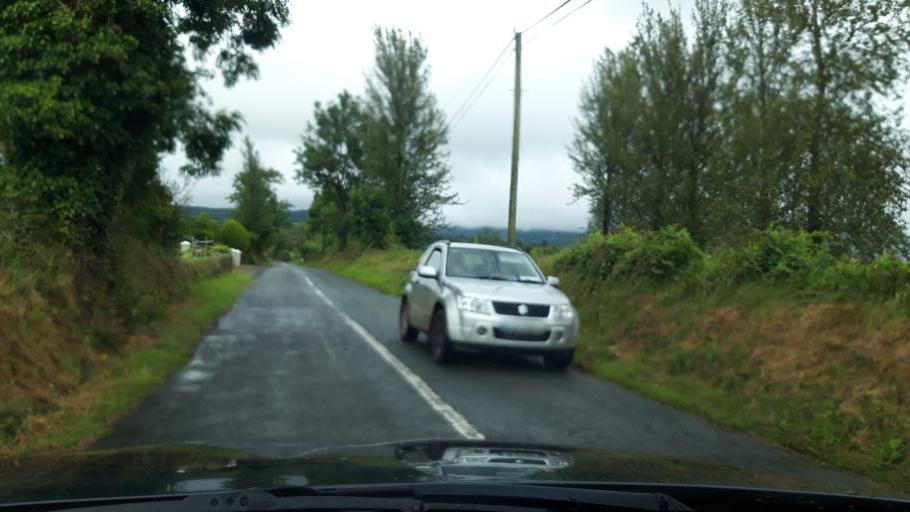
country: IE
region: Munster
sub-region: County Cork
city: Youghal
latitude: 52.1681
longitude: -7.8524
